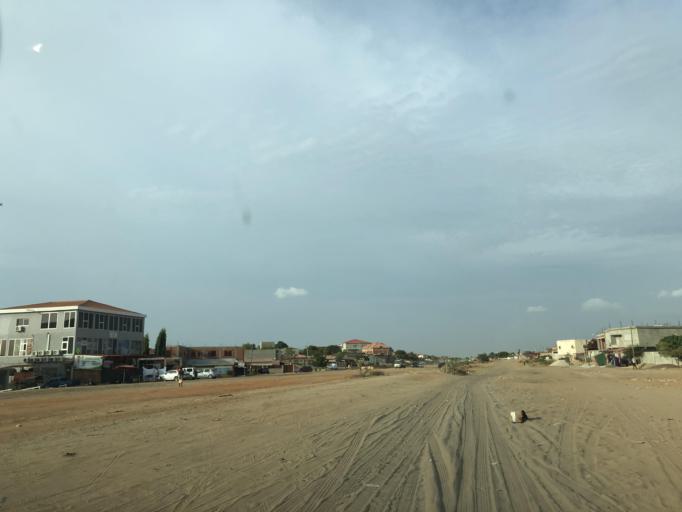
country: AO
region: Luanda
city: Luanda
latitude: -8.9254
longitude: 13.3052
